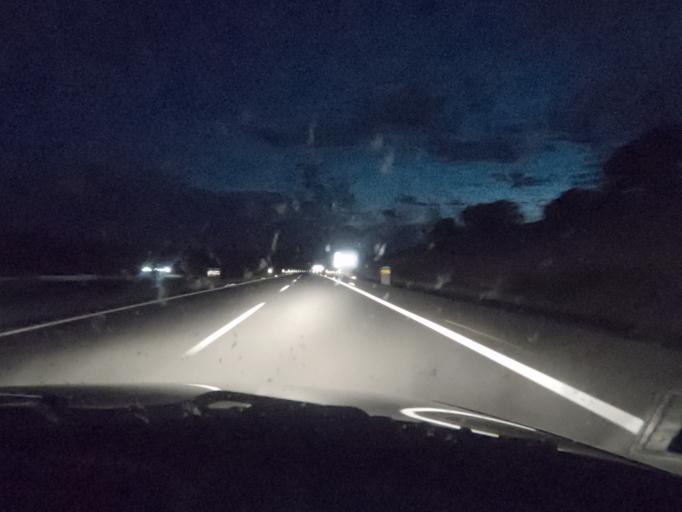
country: ES
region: Extremadura
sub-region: Provincia de Caceres
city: Coria
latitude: 39.9873
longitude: -6.4782
